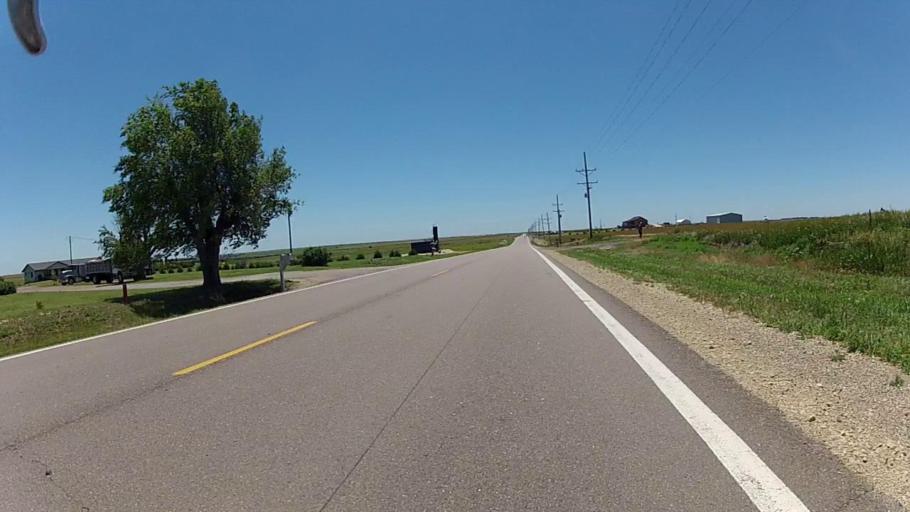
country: US
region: Kansas
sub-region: Kiowa County
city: Greensburg
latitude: 37.5059
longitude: -99.3203
